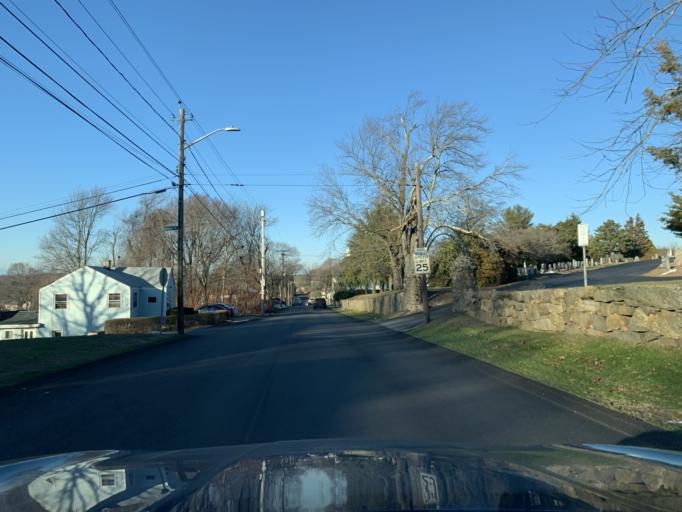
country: US
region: Rhode Island
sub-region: Kent County
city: West Warwick
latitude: 41.6859
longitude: -71.5201
